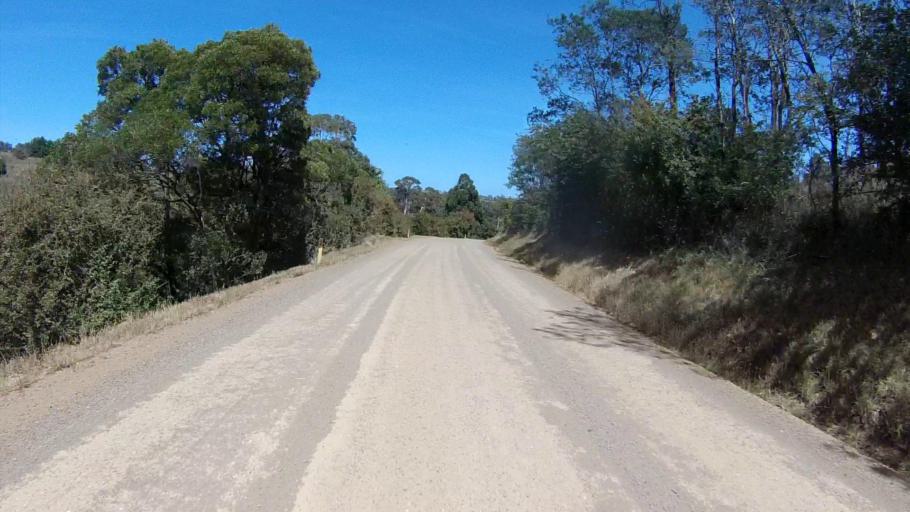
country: AU
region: Tasmania
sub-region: Sorell
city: Sorell
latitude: -42.7566
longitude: 147.6627
